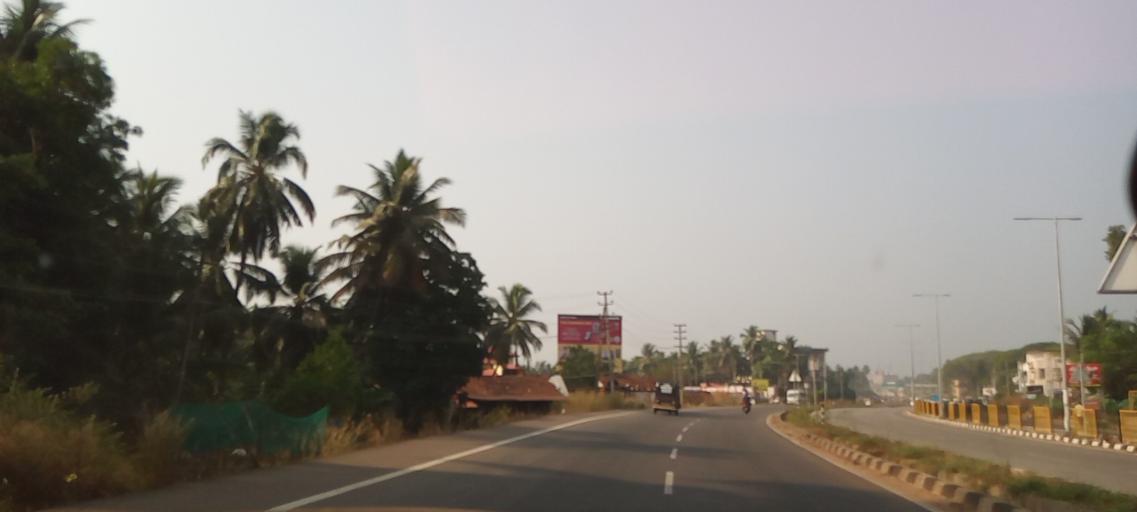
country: IN
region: Karnataka
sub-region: Udupi
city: Coondapoor
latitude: 13.6328
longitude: 74.7011
